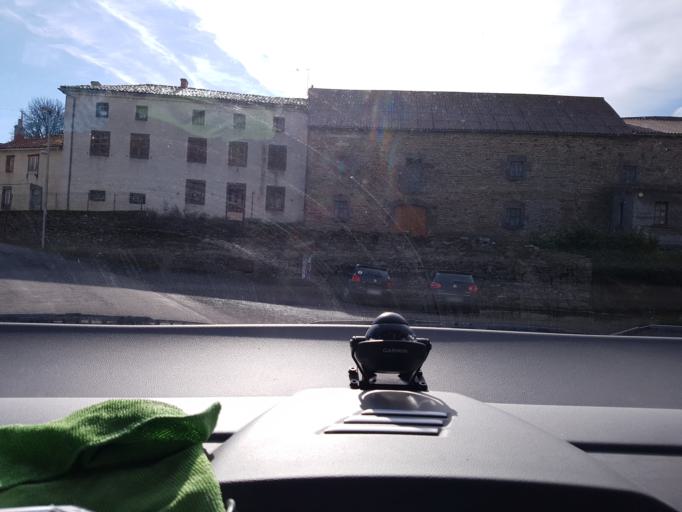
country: FR
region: Auvergne
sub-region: Departement du Cantal
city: Saint-Flour
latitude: 45.1267
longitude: 3.1492
